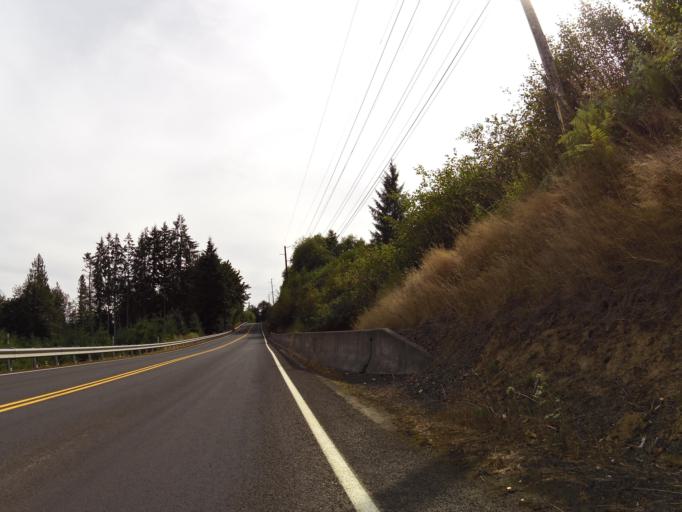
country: US
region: Washington
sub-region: Cowlitz County
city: Castle Rock
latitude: 46.3305
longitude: -122.9298
